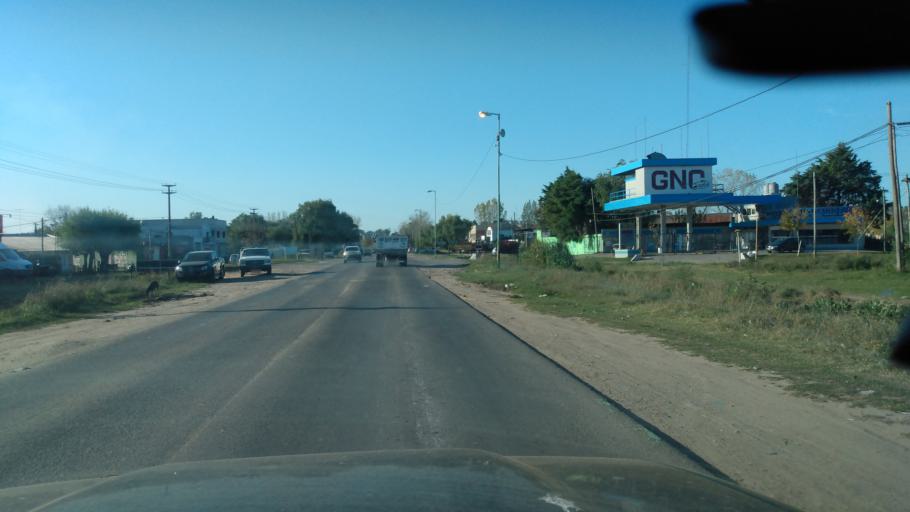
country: AR
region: Buenos Aires
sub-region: Partido de Lujan
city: Lujan
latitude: -34.5411
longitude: -59.1205
